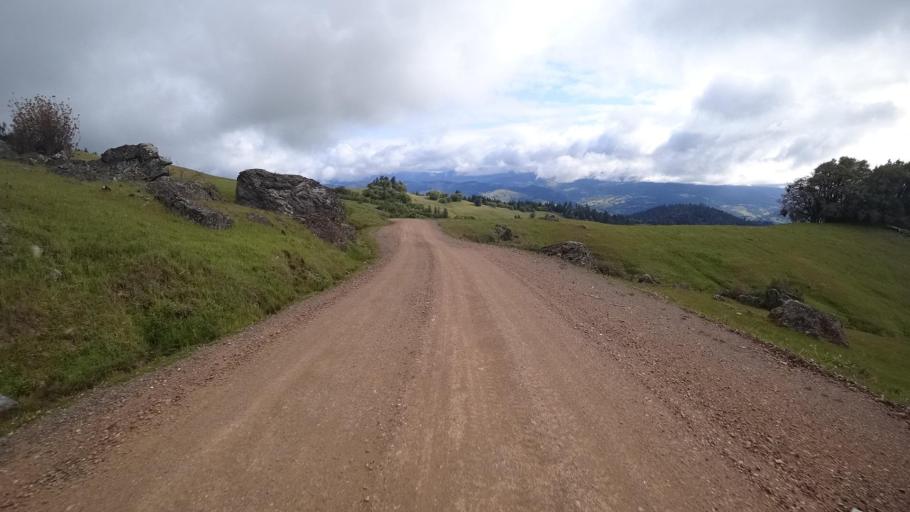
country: US
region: California
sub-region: Humboldt County
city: Redway
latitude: 40.2007
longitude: -123.6939
